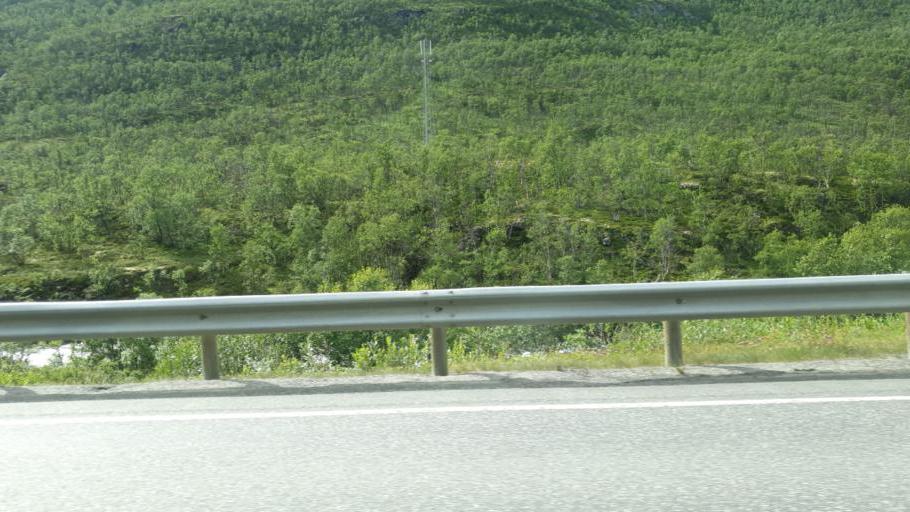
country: NO
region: Sor-Trondelag
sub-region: Oppdal
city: Oppdal
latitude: 62.3190
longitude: 9.6211
